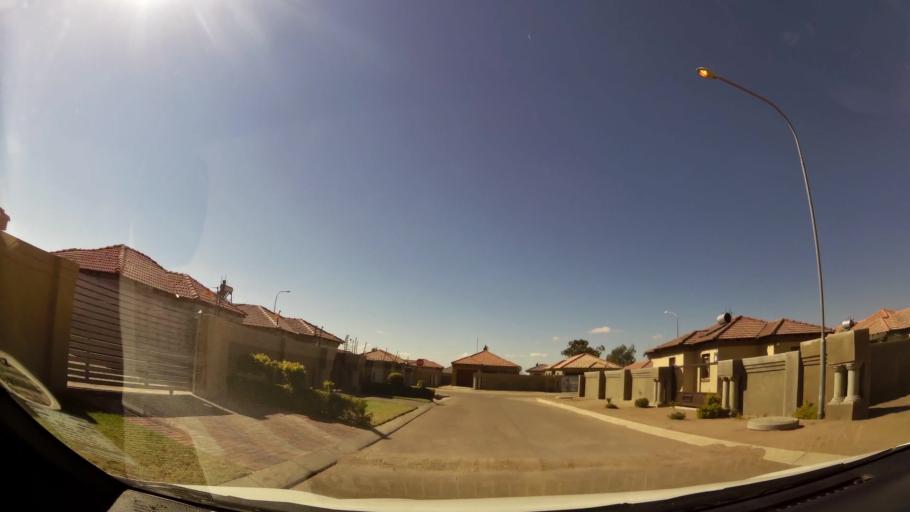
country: ZA
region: Limpopo
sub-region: Capricorn District Municipality
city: Polokwane
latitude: -23.8638
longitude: 29.4248
